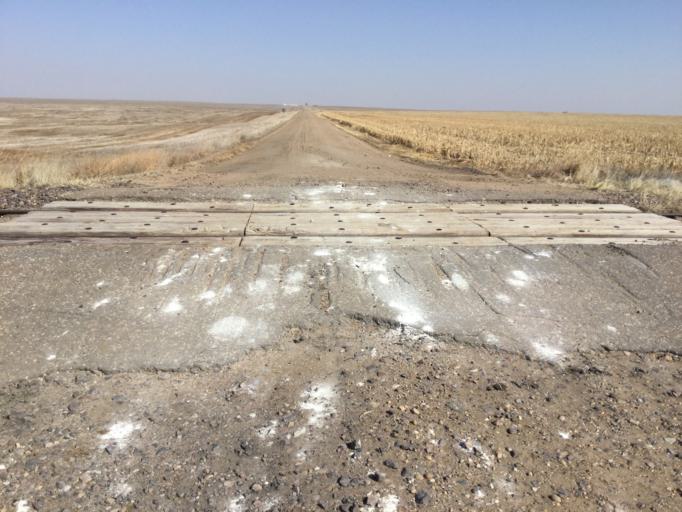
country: US
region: Kansas
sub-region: Rush County
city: La Crosse
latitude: 38.5460
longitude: -99.4017
